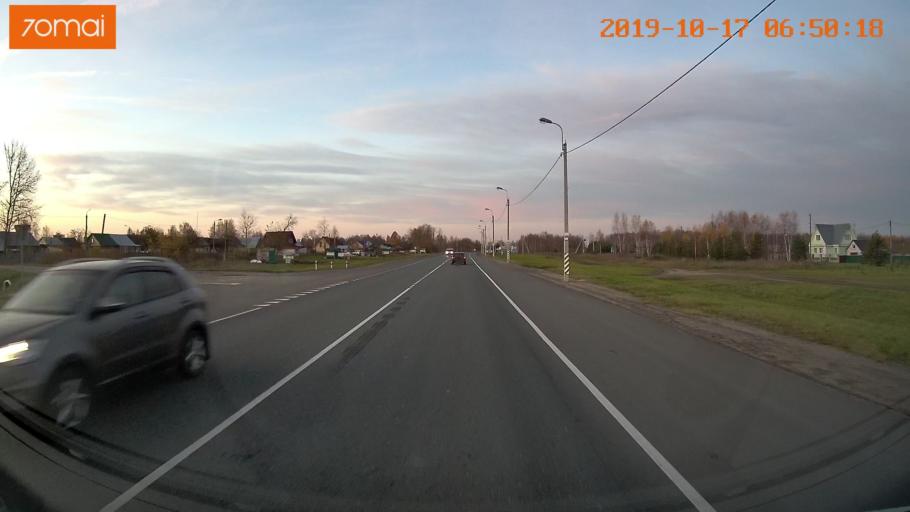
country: RU
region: Vladimir
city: Kideksha
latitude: 56.5049
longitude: 40.5423
